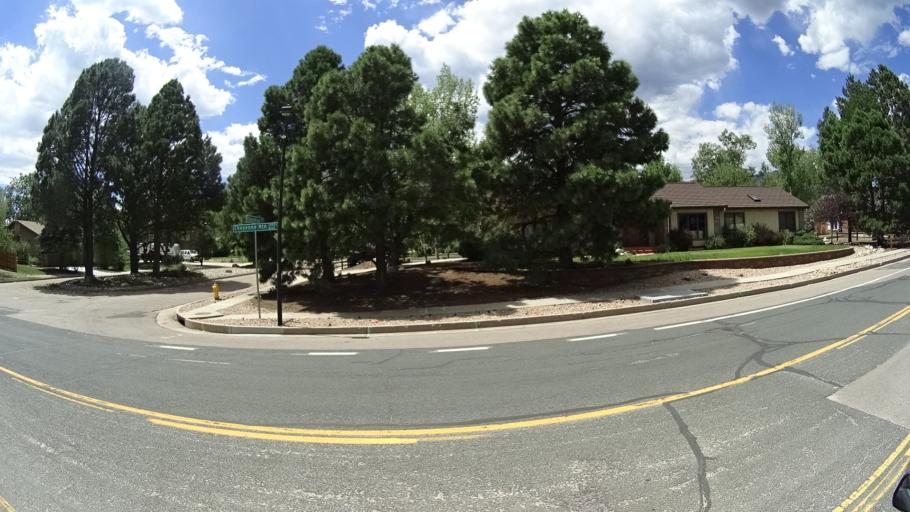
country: US
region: Colorado
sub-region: El Paso County
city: Colorado Springs
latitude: 38.7906
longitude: -104.8252
